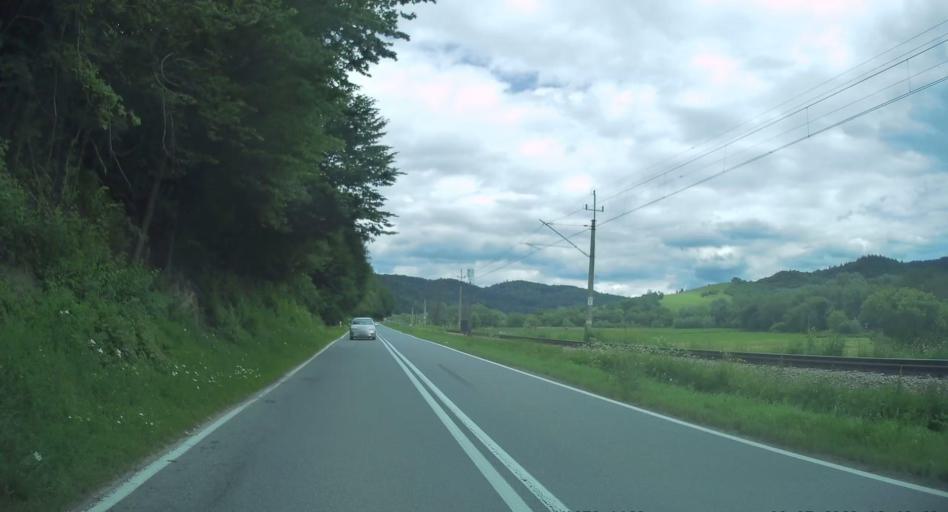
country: PL
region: Lesser Poland Voivodeship
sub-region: Powiat nowosadecki
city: Muszyna
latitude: 49.3412
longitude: 20.8438
